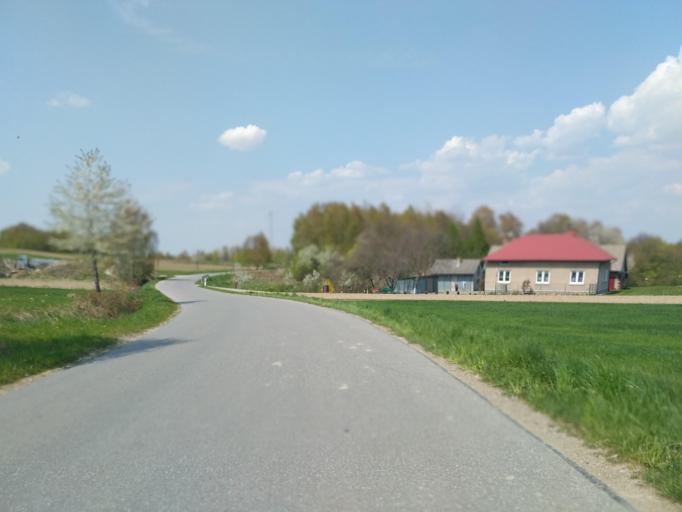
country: PL
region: Subcarpathian Voivodeship
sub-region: Powiat jasielski
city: Osiek Jasielski
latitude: 49.6768
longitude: 21.5186
